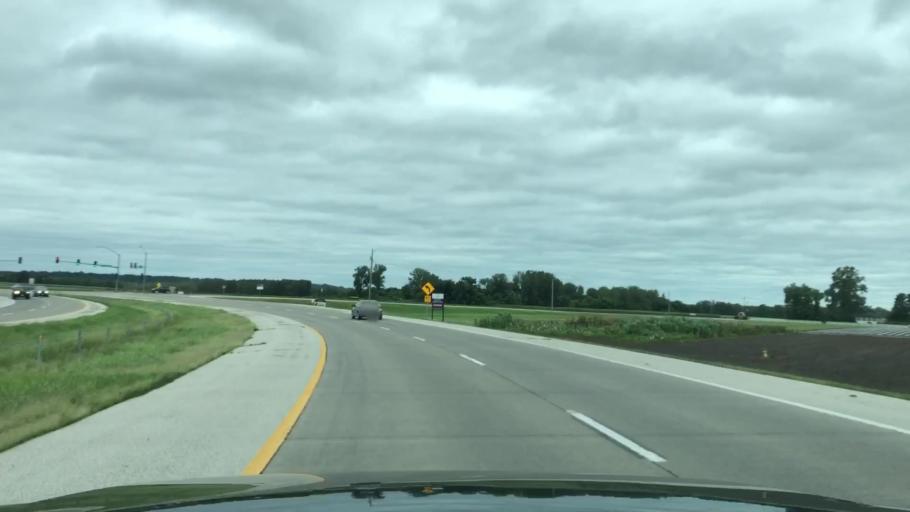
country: US
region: Missouri
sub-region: Saint Charles County
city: Saint Charles
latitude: 38.7267
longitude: -90.4984
